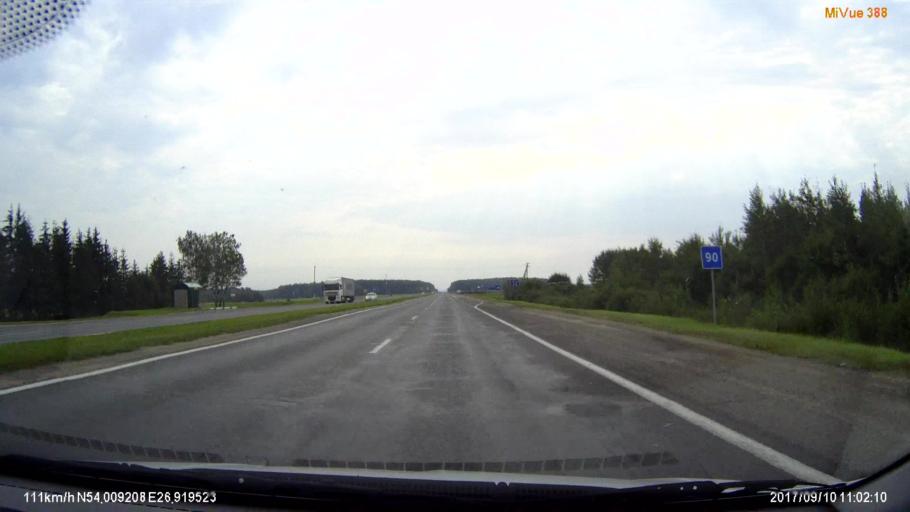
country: BY
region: Minsk
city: Rakaw
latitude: 54.0092
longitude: 26.9195
